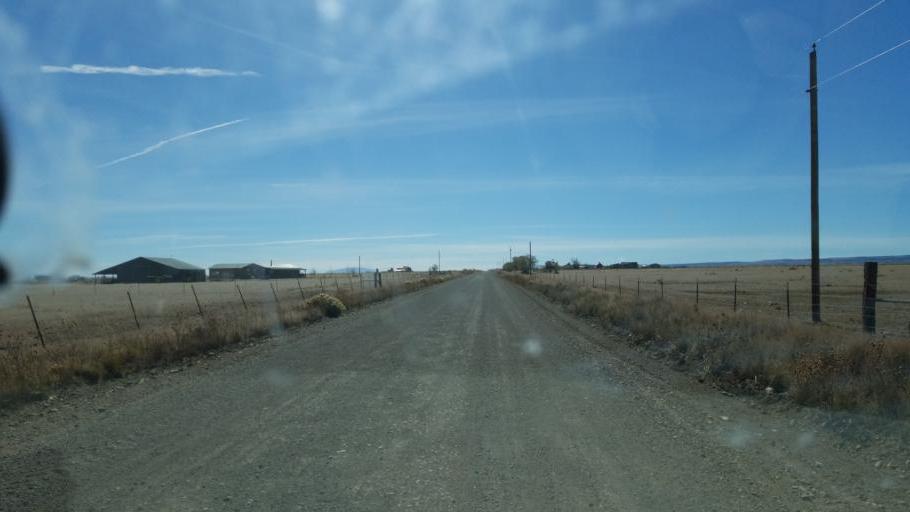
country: US
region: Colorado
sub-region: Rio Grande County
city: Monte Vista
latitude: 37.3837
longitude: -106.1494
